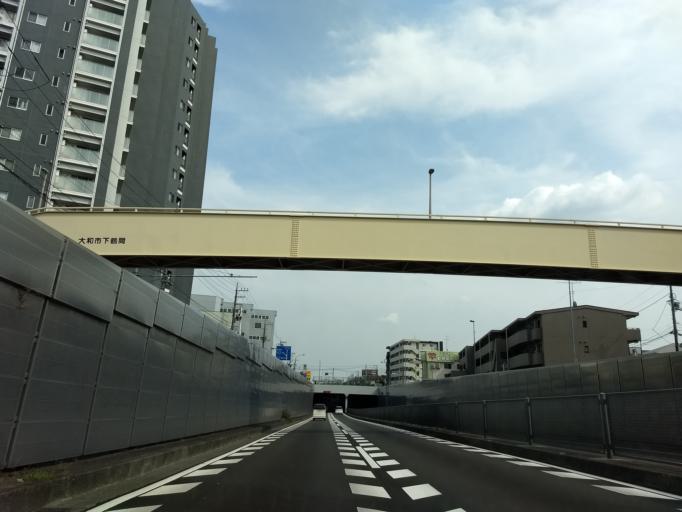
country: JP
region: Tokyo
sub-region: Machida-shi
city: Machida
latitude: 35.5176
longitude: 139.4547
